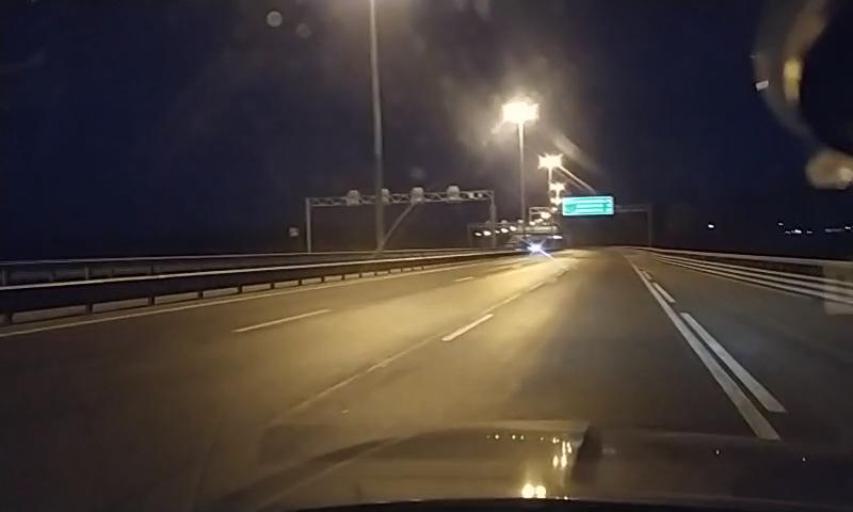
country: RU
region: St.-Petersburg
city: Pesochnyy
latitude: 60.0678
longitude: 30.1384
